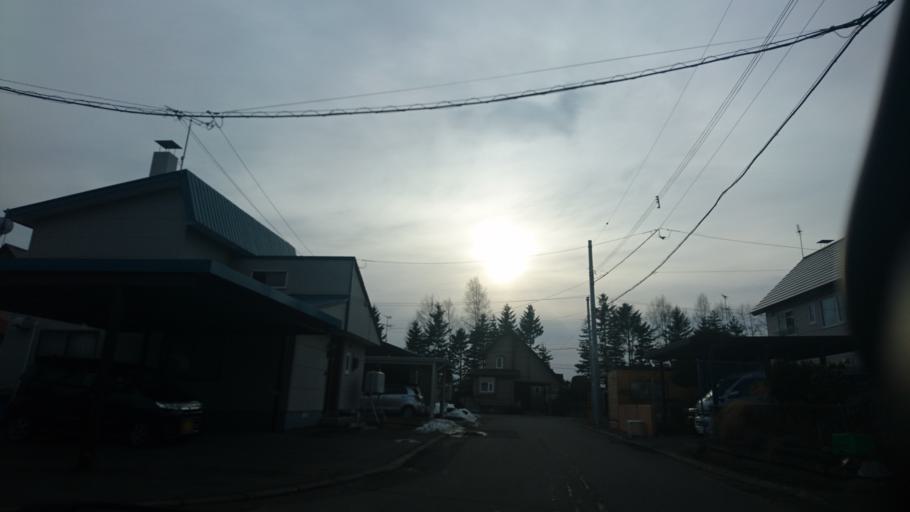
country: JP
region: Hokkaido
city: Otofuke
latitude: 42.9930
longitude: 143.1901
